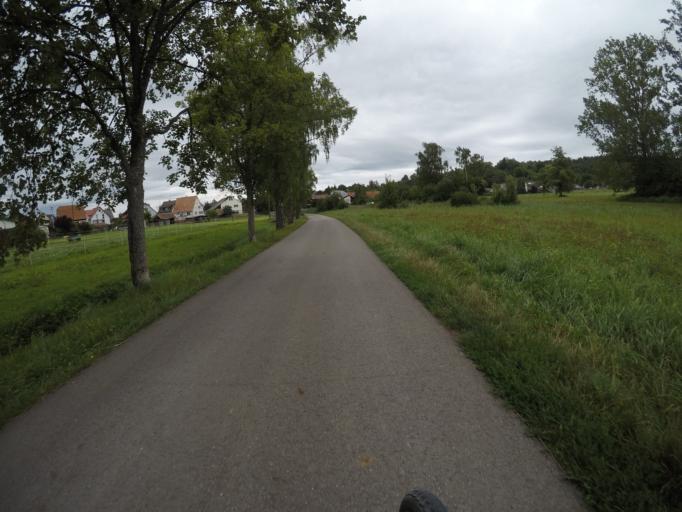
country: DE
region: Baden-Wuerttemberg
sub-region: Regierungsbezirk Stuttgart
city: Gartringen
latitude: 48.6240
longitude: 8.9247
